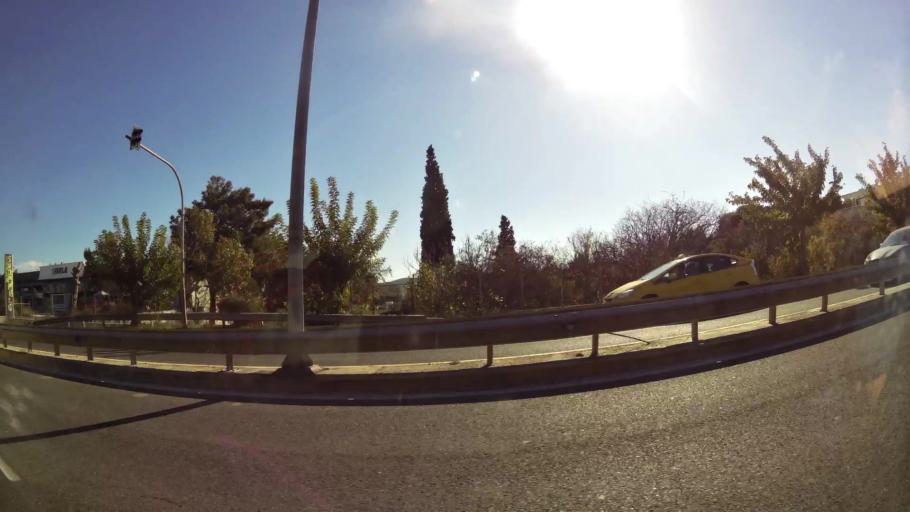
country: GR
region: Attica
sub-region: Nomarchia Anatolikis Attikis
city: Pallini
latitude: 38.0039
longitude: 23.8951
